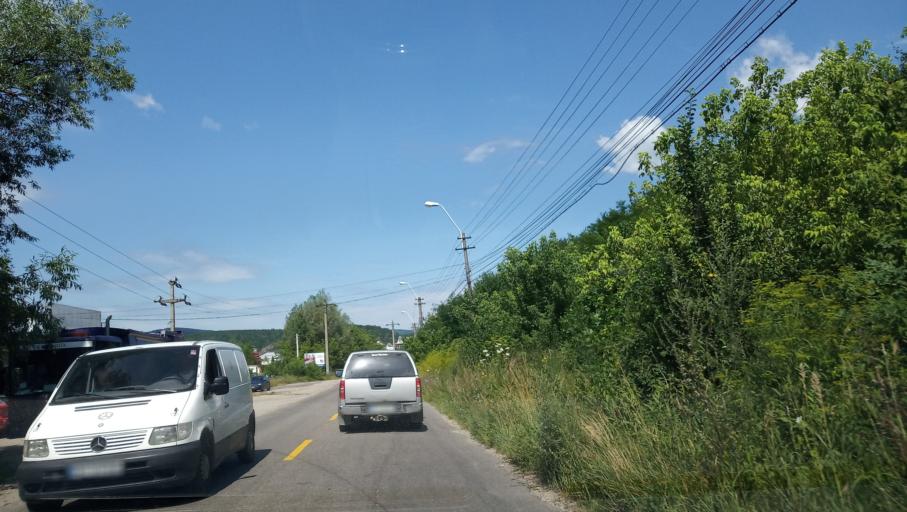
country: RO
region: Hunedoara
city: Hunedoara
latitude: 45.7365
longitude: 22.9081
